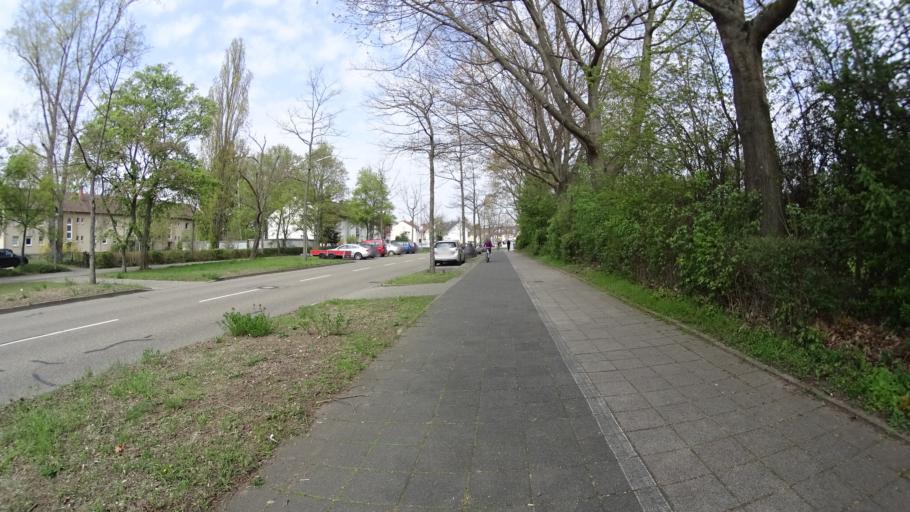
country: DE
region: Baden-Wuerttemberg
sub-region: Karlsruhe Region
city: Karlsruhe
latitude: 49.0325
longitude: 8.3705
